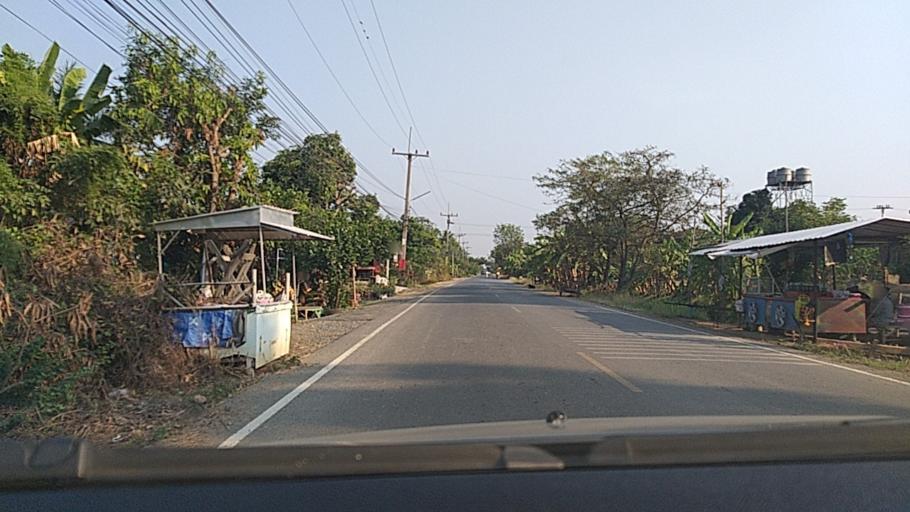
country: TH
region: Sing Buri
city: Sing Buri
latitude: 14.8384
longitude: 100.3946
